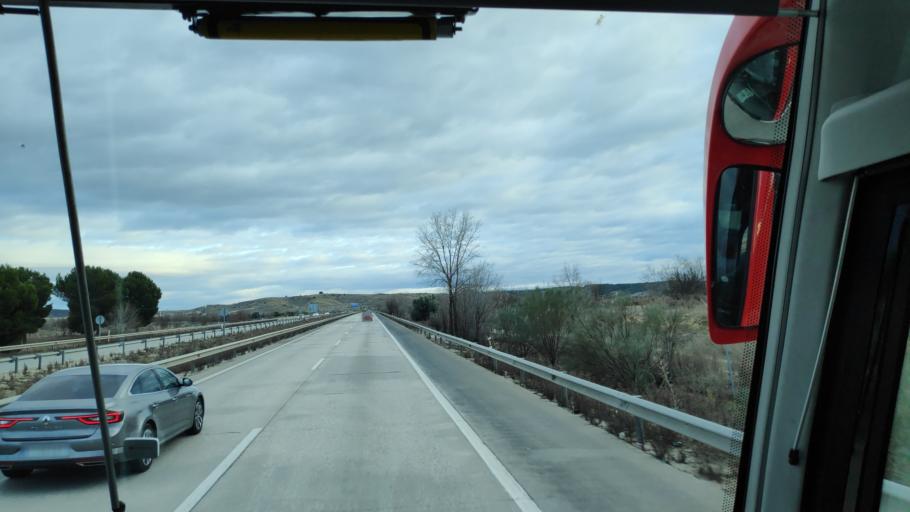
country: ES
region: Madrid
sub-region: Provincia de Madrid
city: Vaciamadrid
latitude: 40.3050
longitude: -3.4881
